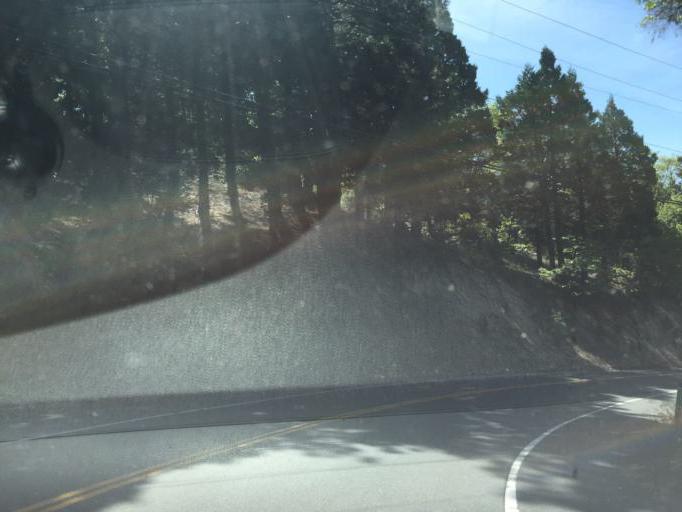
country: US
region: California
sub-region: San Bernardino County
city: Crestline
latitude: 34.2339
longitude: -117.2418
